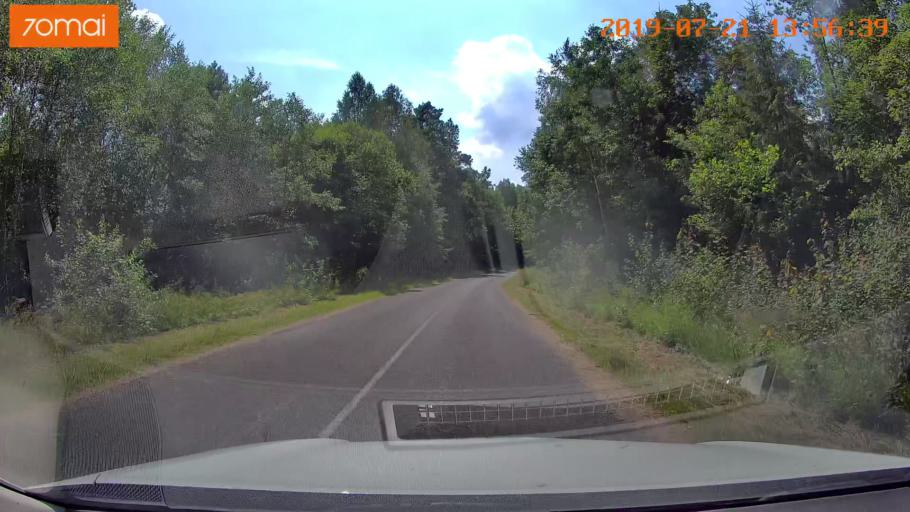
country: BY
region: Grodnenskaya
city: Lyubcha
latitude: 53.7775
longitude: 26.0984
